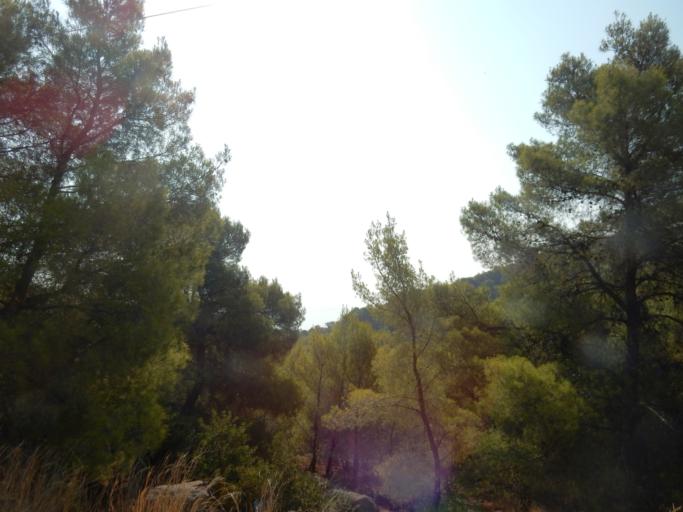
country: GR
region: Attica
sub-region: Nomos Piraios
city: Vathi
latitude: 37.7224
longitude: 23.5221
